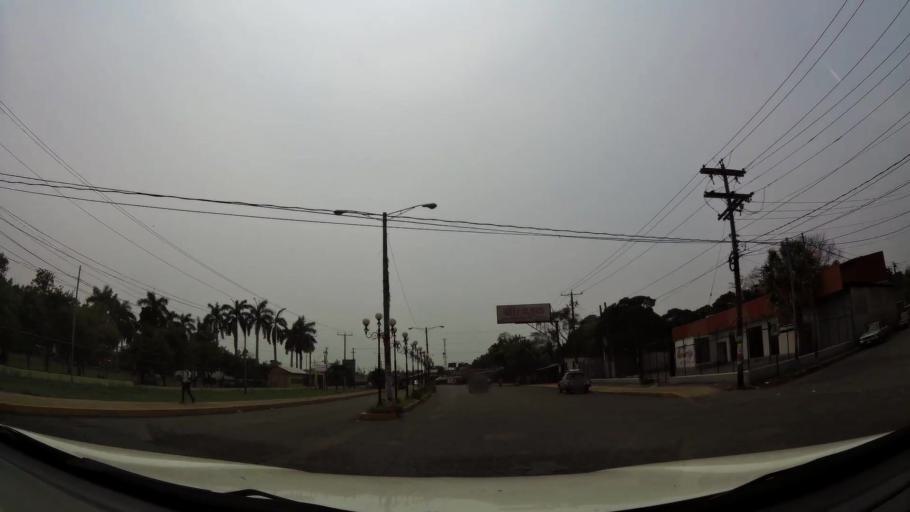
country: NI
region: Chinandega
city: Chinandega
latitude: 12.6249
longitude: -87.1233
